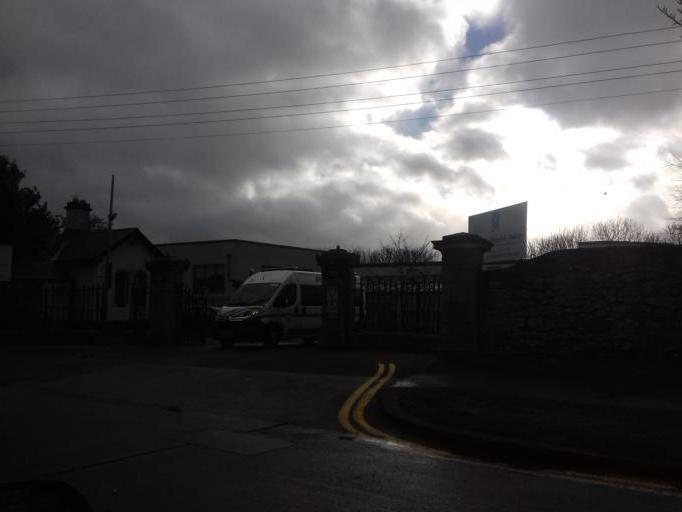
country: IE
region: Leinster
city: Raheny
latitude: 53.3827
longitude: -6.1800
